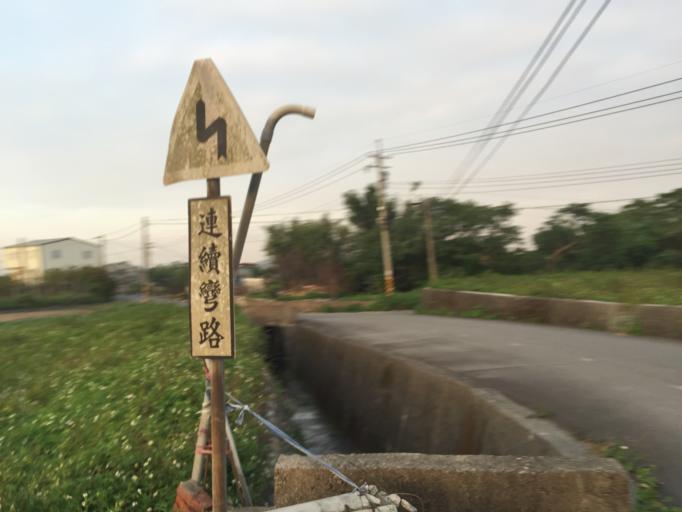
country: TW
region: Taiwan
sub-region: Miaoli
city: Miaoli
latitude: 24.4902
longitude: 120.7766
